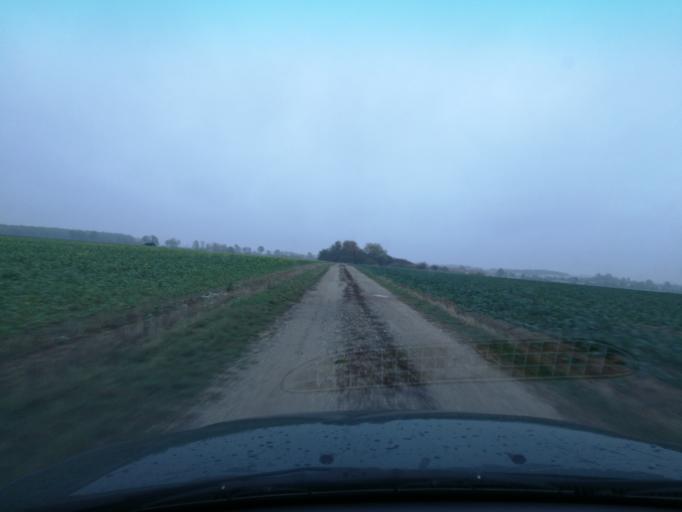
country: DE
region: Bavaria
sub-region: Regierungsbezirk Mittelfranken
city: Obermichelbach
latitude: 49.5406
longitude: 10.9086
